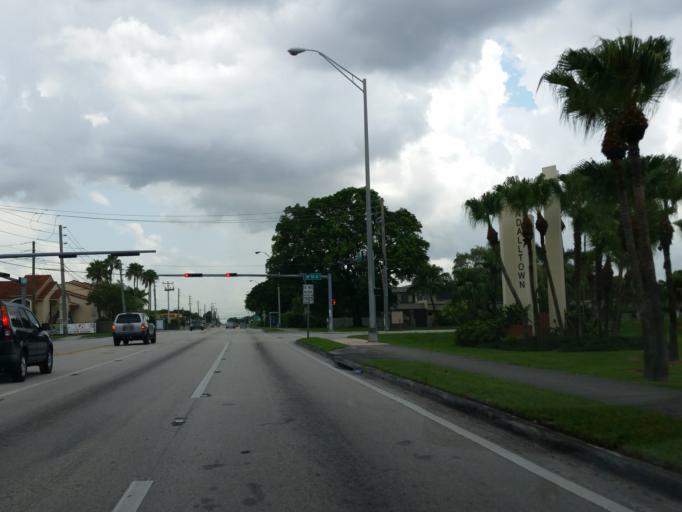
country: US
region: Florida
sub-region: Miami-Dade County
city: Sunset
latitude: 25.6967
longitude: -80.3660
